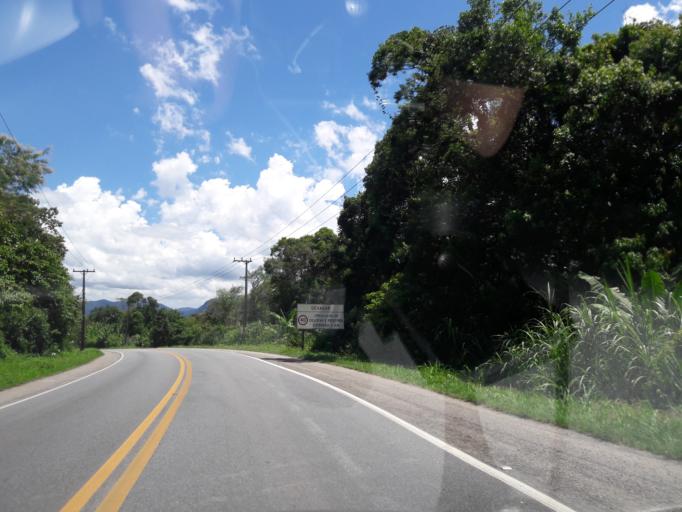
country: BR
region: Parana
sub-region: Antonina
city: Antonina
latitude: -25.4633
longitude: -48.8237
